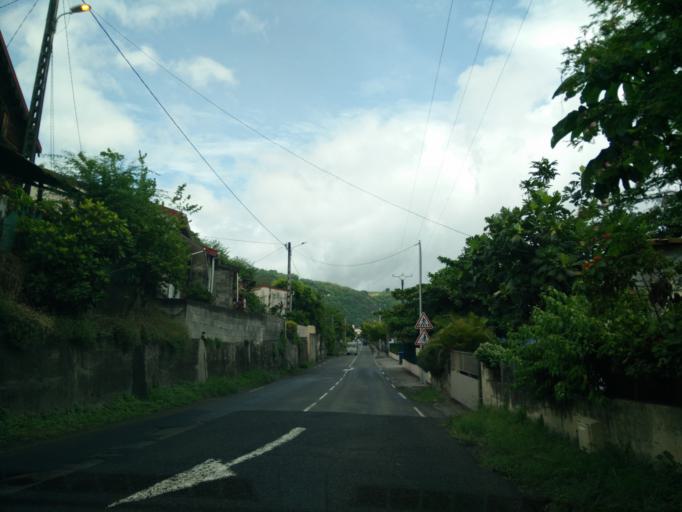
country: MQ
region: Martinique
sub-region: Martinique
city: Saint-Pierre
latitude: 14.7536
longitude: -61.1821
